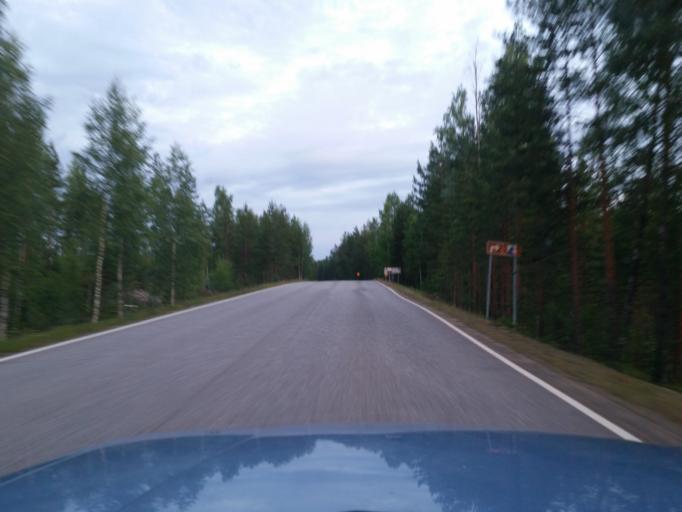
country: FI
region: Southern Savonia
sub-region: Savonlinna
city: Sulkava
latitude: 61.8026
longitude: 28.4107
